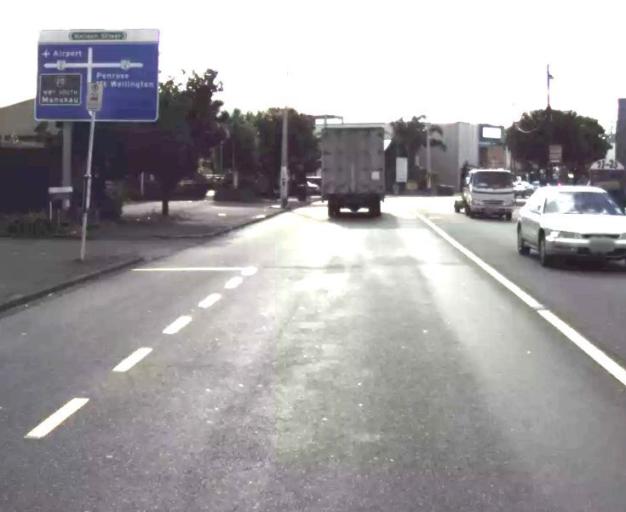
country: NZ
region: Auckland
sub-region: Auckland
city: Mangere
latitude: -36.9285
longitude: 174.7863
